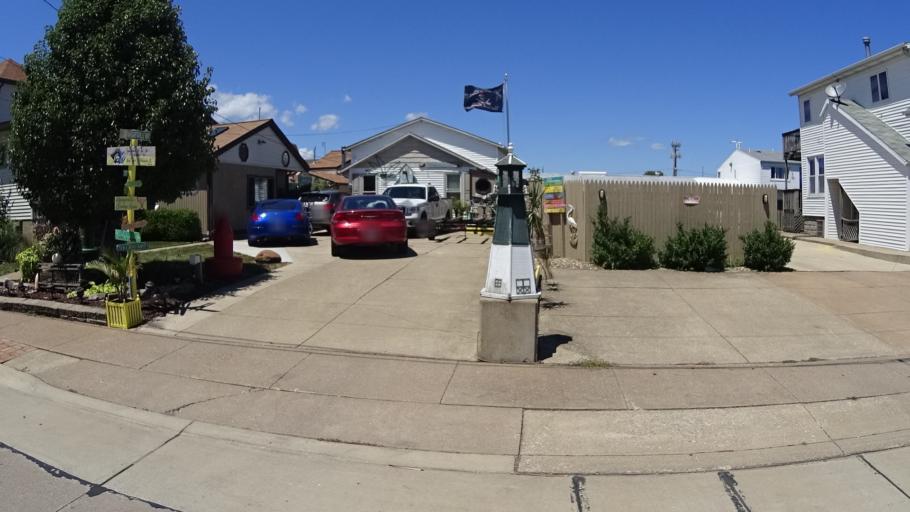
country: US
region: Ohio
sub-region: Erie County
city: Sandusky
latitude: 41.4563
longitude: -82.6991
